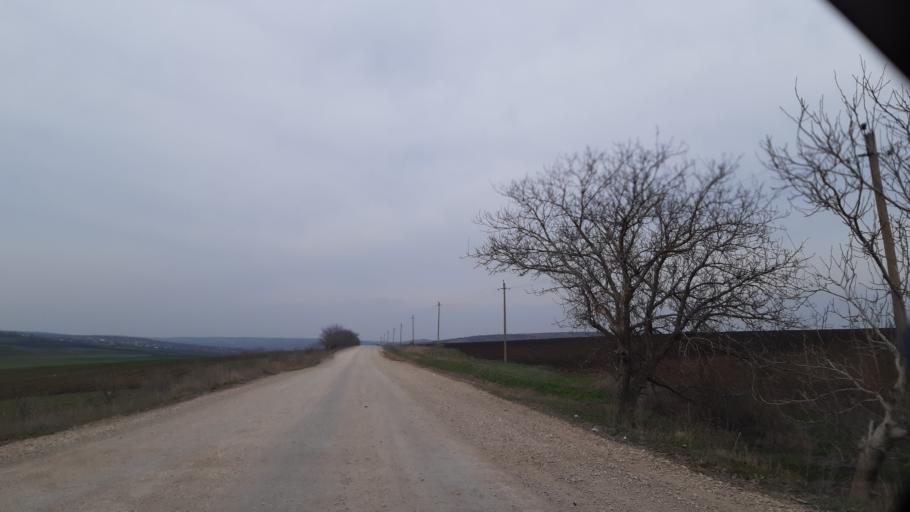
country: MD
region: Soldanesti
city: Soldanesti
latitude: 47.6094
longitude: 28.6541
